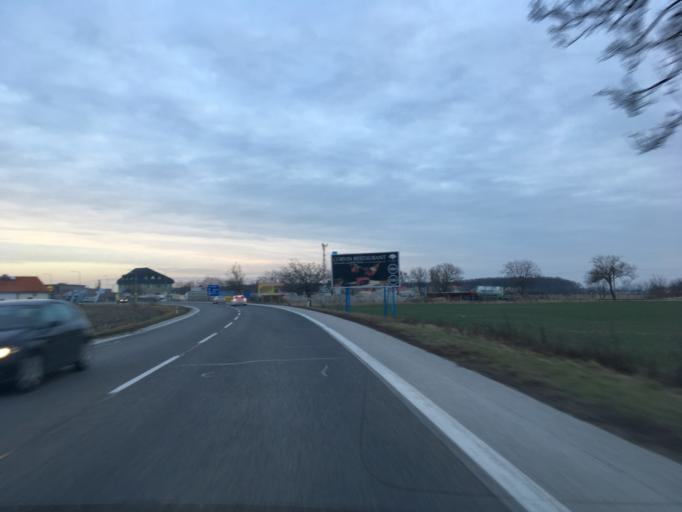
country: SK
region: Trnavsky
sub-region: Okres Dunajska Streda
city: Velky Meder
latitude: 47.8654
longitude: 17.7574
